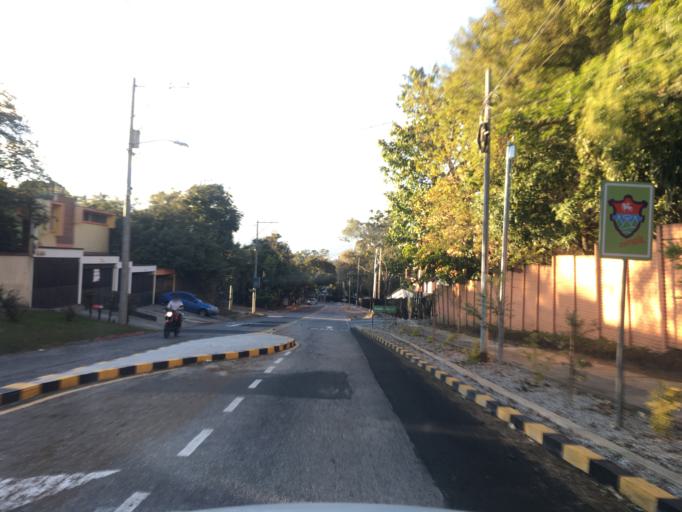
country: GT
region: Guatemala
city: Santa Catarina Pinula
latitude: 14.6037
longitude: -90.4894
